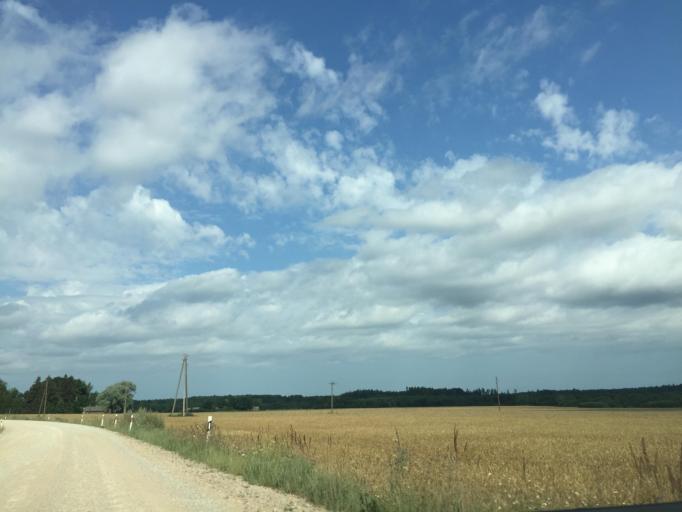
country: LV
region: Kandava
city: Kandava
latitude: 56.9966
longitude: 22.8885
